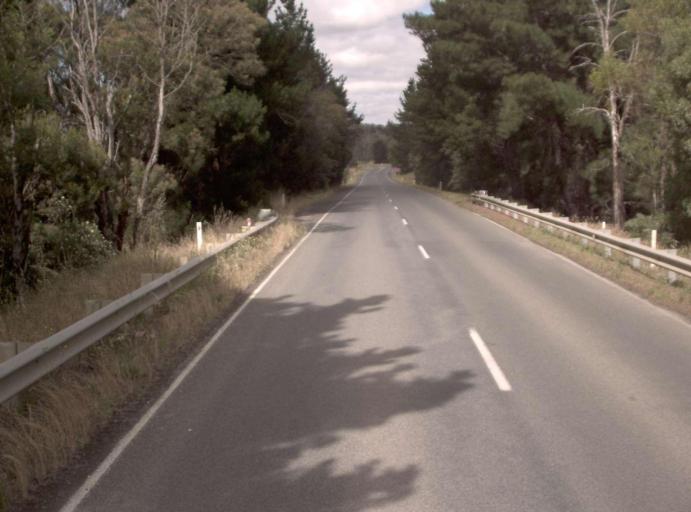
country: AU
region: Victoria
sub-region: Latrobe
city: Morwell
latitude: -38.1985
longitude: 146.4437
